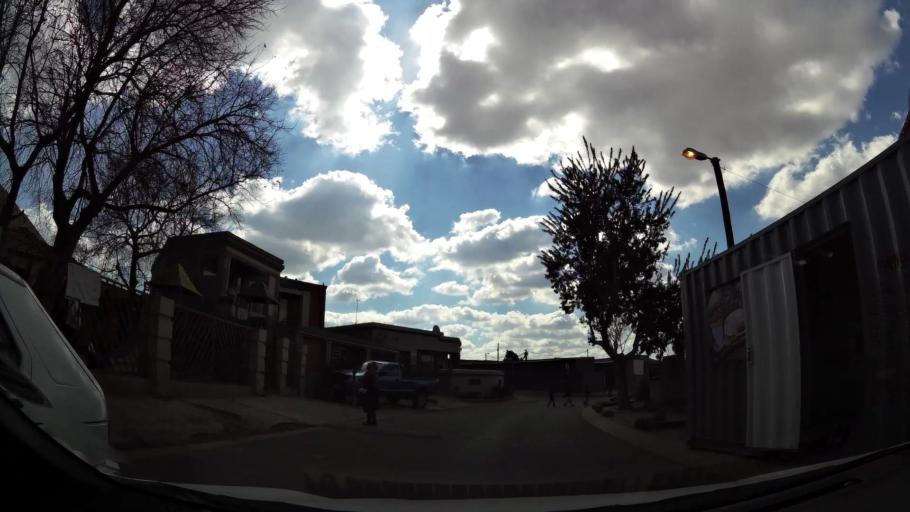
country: ZA
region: Gauteng
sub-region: City of Tshwane Metropolitan Municipality
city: Cullinan
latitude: -25.7031
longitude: 28.3949
